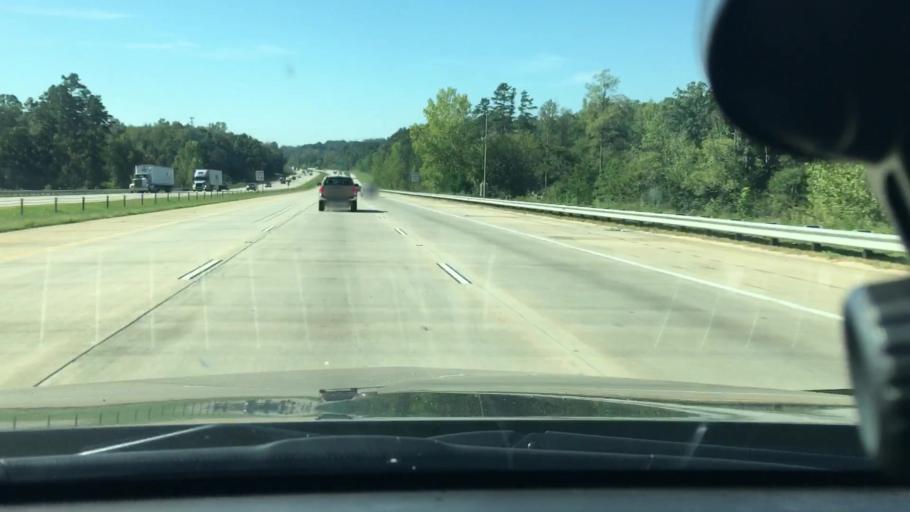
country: US
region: North Carolina
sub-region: Gaston County
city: Mount Holly
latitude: 35.3136
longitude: -80.9484
